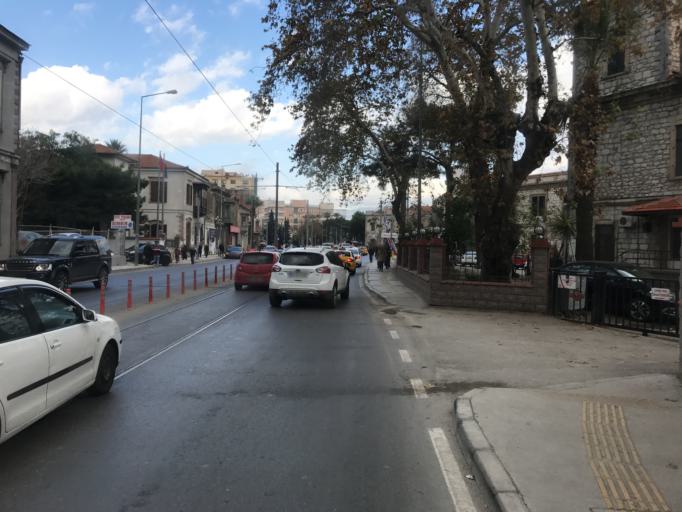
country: TR
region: Izmir
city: Izmir
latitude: 38.4373
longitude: 27.1476
